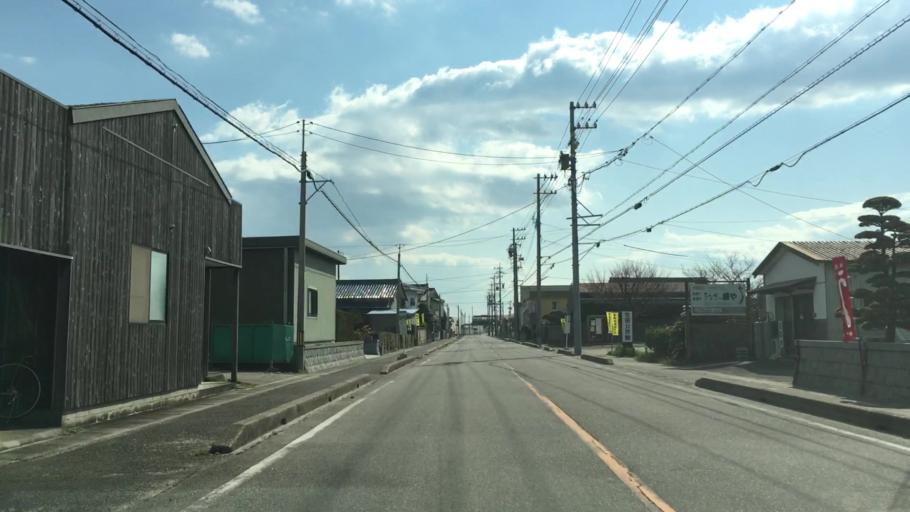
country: JP
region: Aichi
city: Ishiki
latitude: 34.7883
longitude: 137.0329
